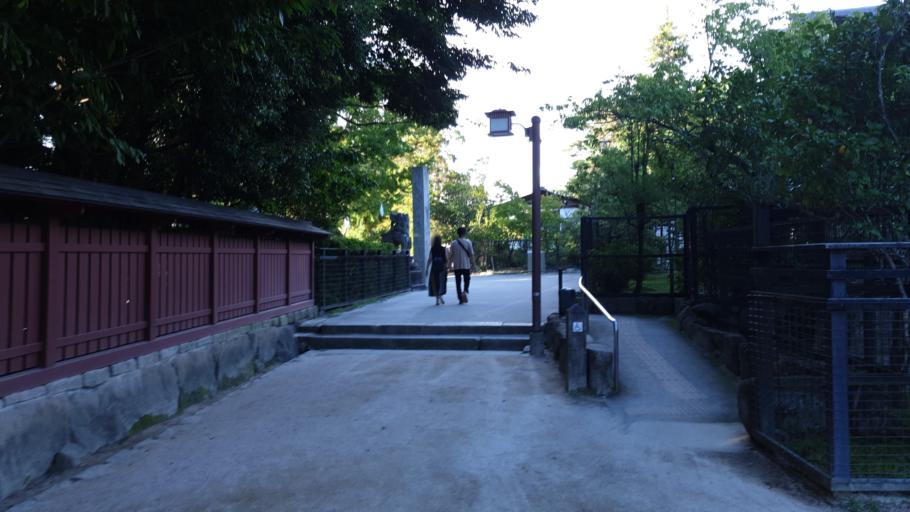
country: JP
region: Hiroshima
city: Miyajima
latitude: 34.2955
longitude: 132.3204
